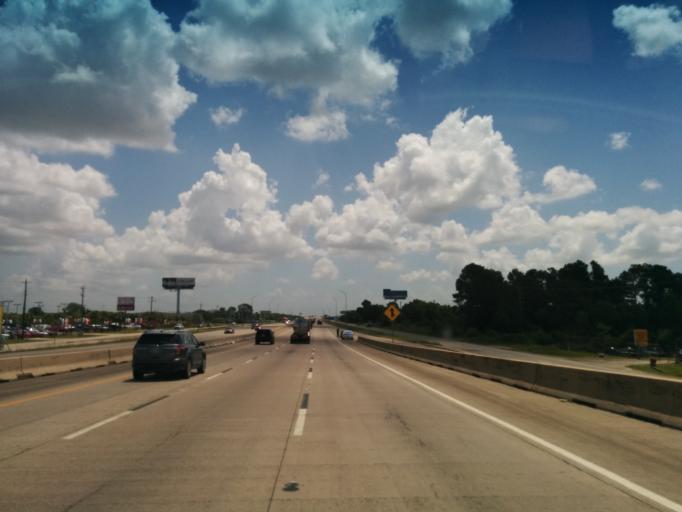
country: US
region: Texas
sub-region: Harris County
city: Baytown
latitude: 29.8051
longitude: -94.9785
